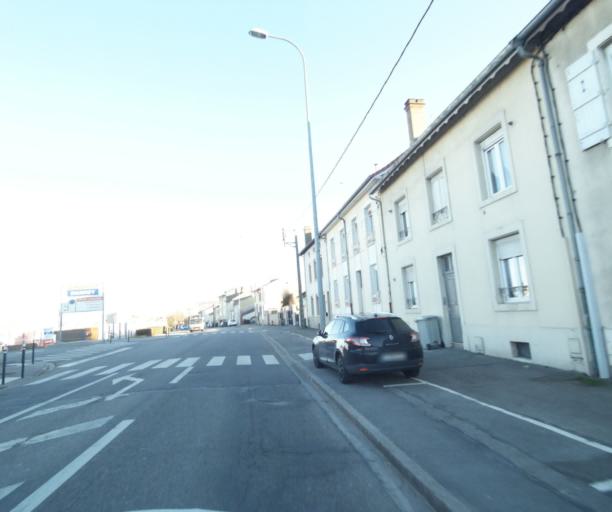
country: FR
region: Lorraine
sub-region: Departement de Meurthe-et-Moselle
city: Laneuveville-devant-Nancy
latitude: 48.6611
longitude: 6.2228
